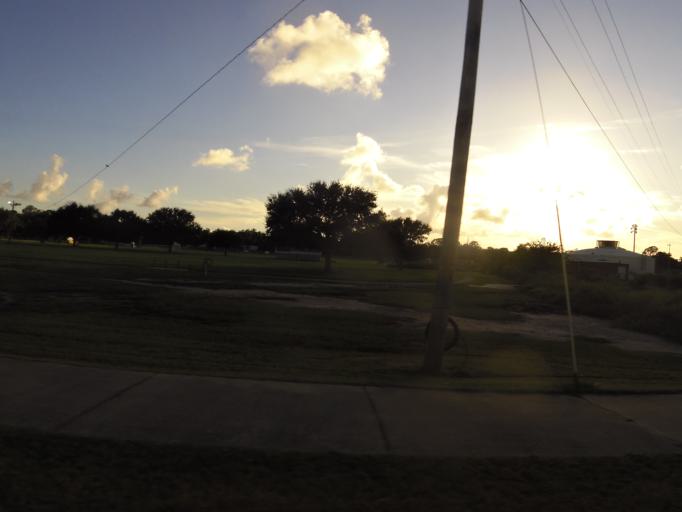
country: US
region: Georgia
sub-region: Glynn County
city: Brunswick
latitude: 31.1508
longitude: -81.4775
